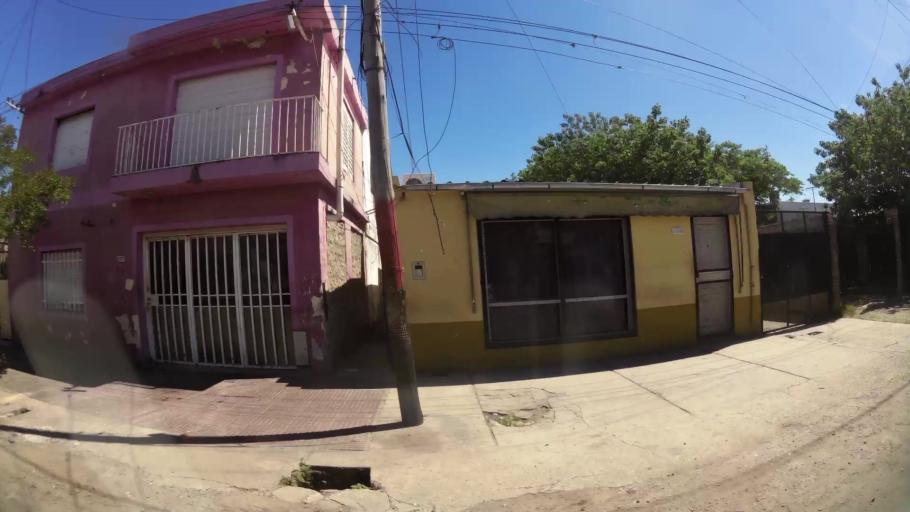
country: AR
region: Santa Fe
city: Perez
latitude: -32.9650
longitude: -60.7159
